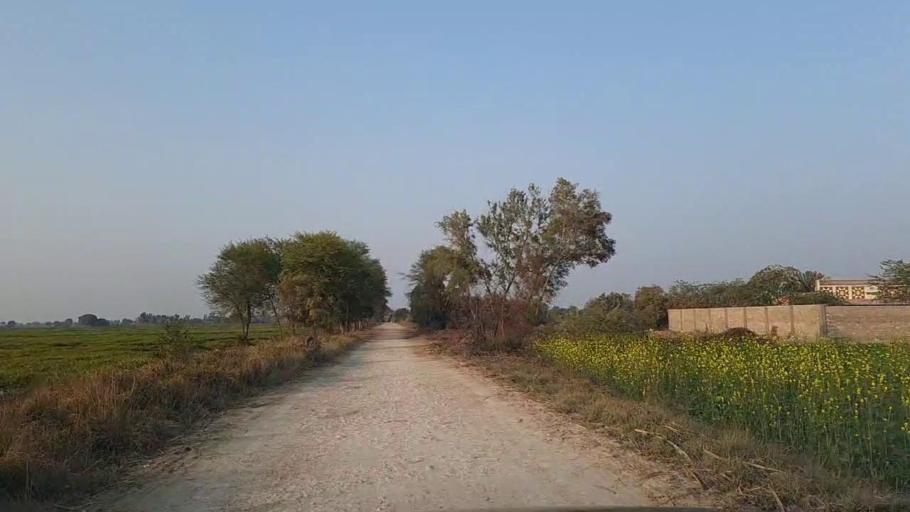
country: PK
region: Sindh
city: Daur
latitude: 26.4302
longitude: 68.3937
